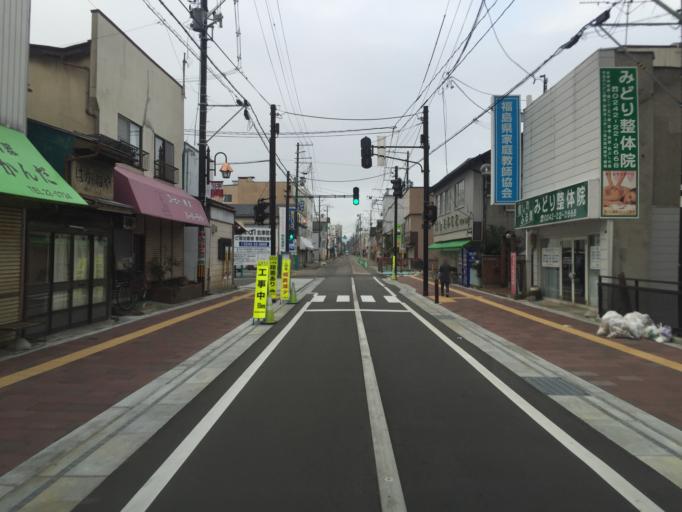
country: JP
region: Fukushima
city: Kitakata
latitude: 37.5065
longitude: 139.9310
